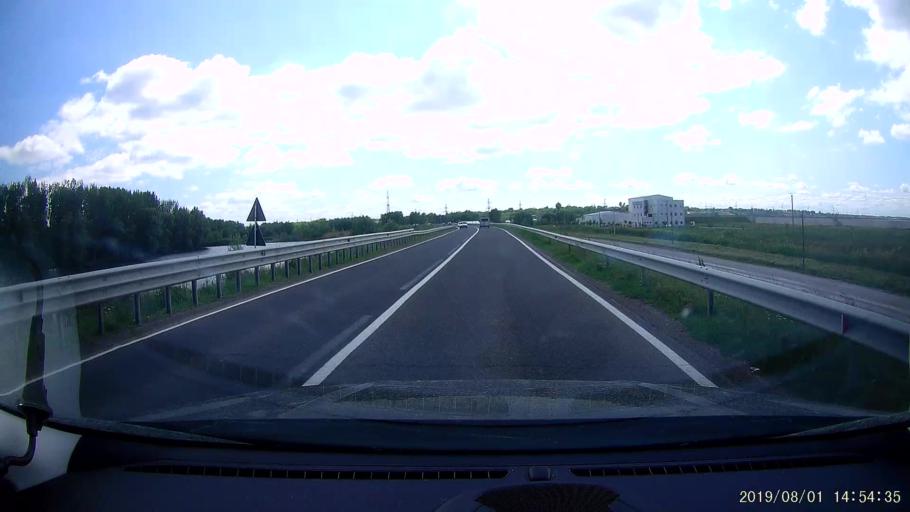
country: RO
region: Braila
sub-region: Municipiul Braila
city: Braila
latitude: 45.3162
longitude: 27.9865
